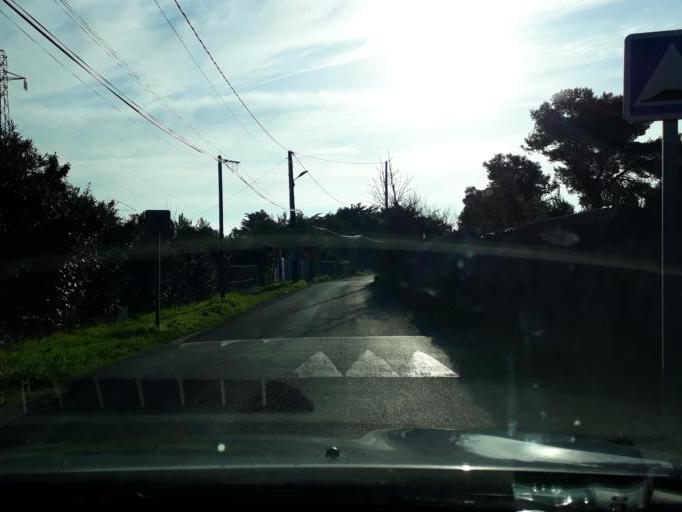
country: FR
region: Languedoc-Roussillon
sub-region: Departement de l'Herault
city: Marseillan
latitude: 43.3226
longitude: 3.5428
